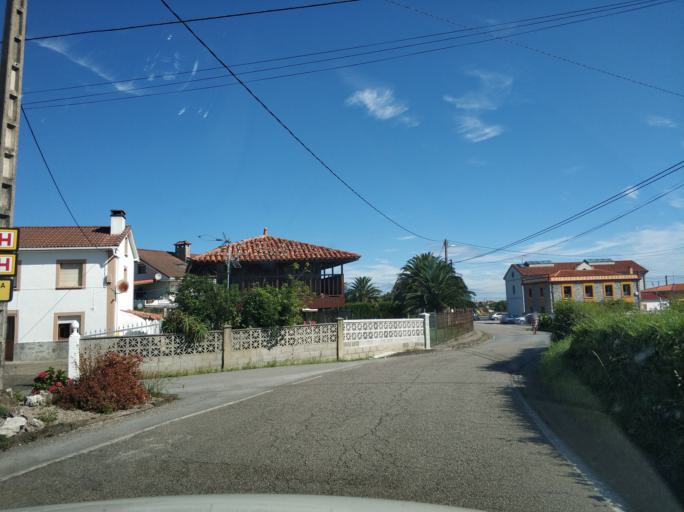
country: ES
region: Asturias
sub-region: Province of Asturias
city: Cudillero
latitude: 43.5735
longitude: -6.2385
